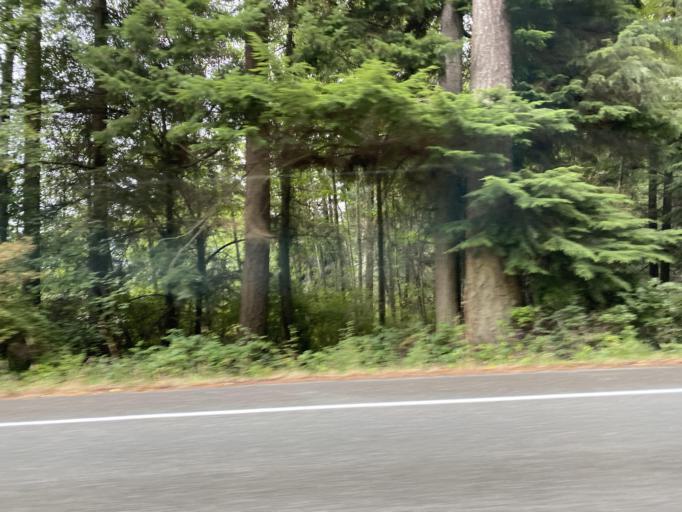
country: US
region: Washington
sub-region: Island County
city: Coupeville
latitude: 48.2171
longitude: -122.6385
